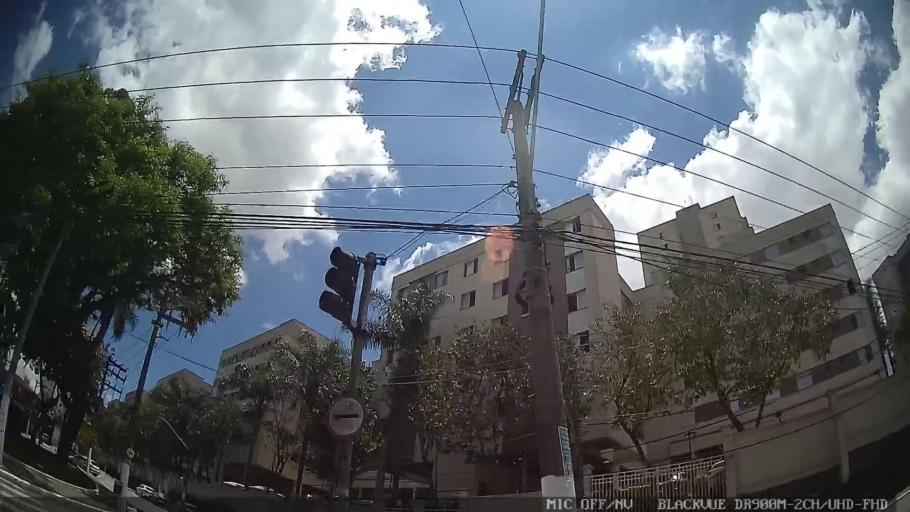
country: BR
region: Sao Paulo
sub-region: Diadema
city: Diadema
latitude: -23.6508
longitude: -46.6475
